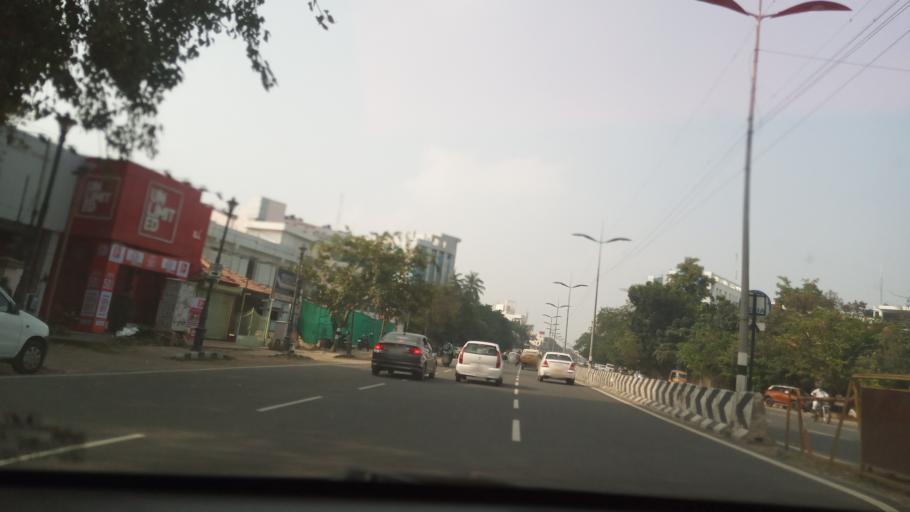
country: IN
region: Tamil Nadu
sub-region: Coimbatore
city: Coimbatore
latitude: 11.0078
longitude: 76.9783
